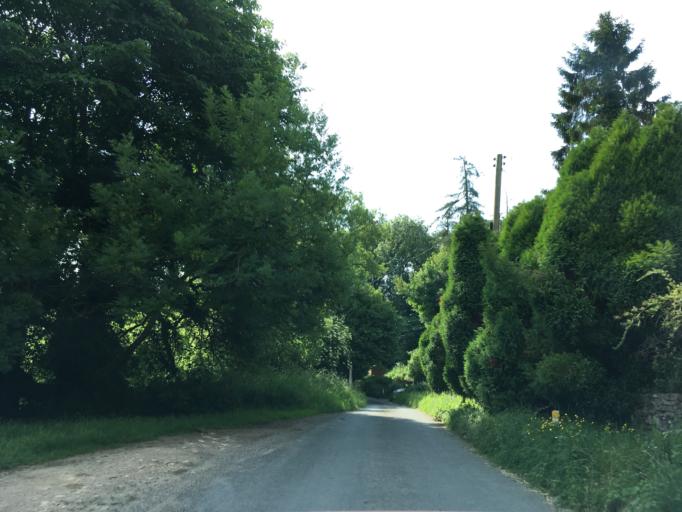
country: GB
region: England
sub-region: Gloucestershire
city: Brimscombe
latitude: 51.7139
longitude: -2.1679
